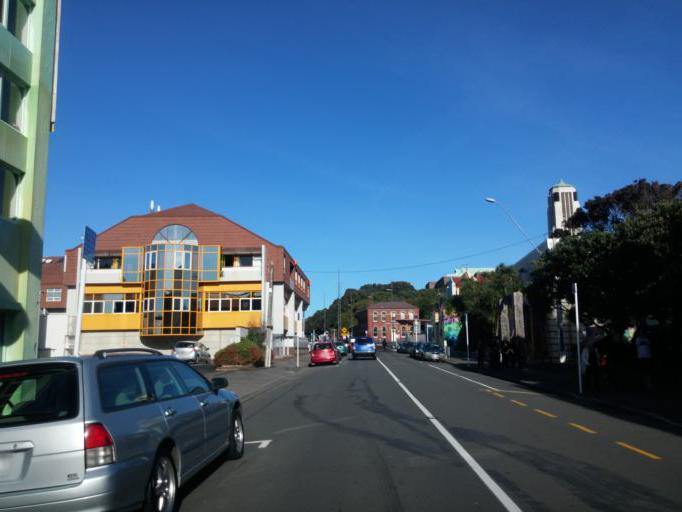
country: NZ
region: Wellington
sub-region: Wellington City
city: Wellington
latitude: -41.2976
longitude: 174.7789
